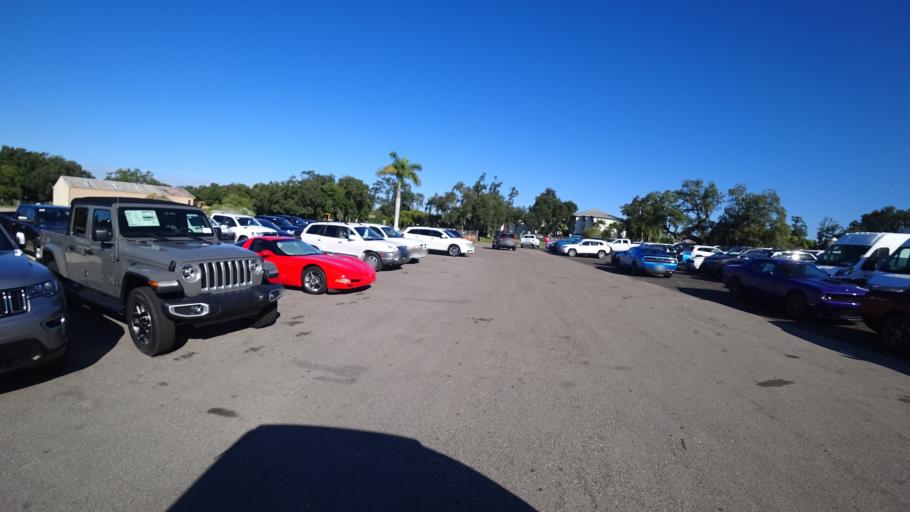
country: US
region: Florida
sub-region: Manatee County
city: West Samoset
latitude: 27.4764
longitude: -82.5652
